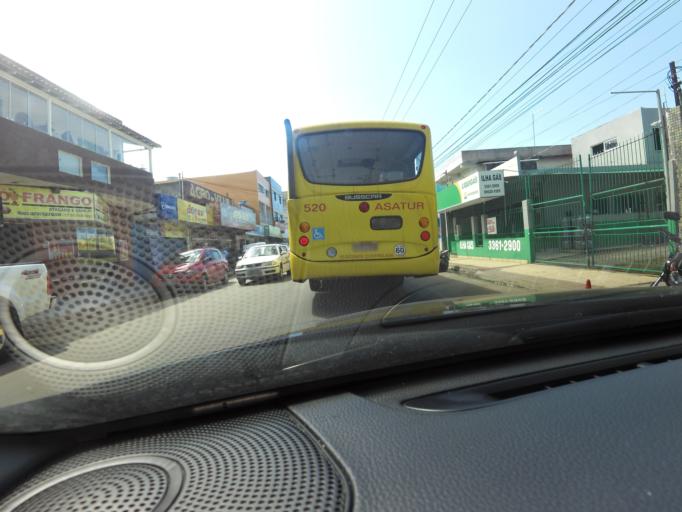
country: BR
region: Espirito Santo
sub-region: Guarapari
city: Guarapari
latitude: -20.6433
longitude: -40.4864
